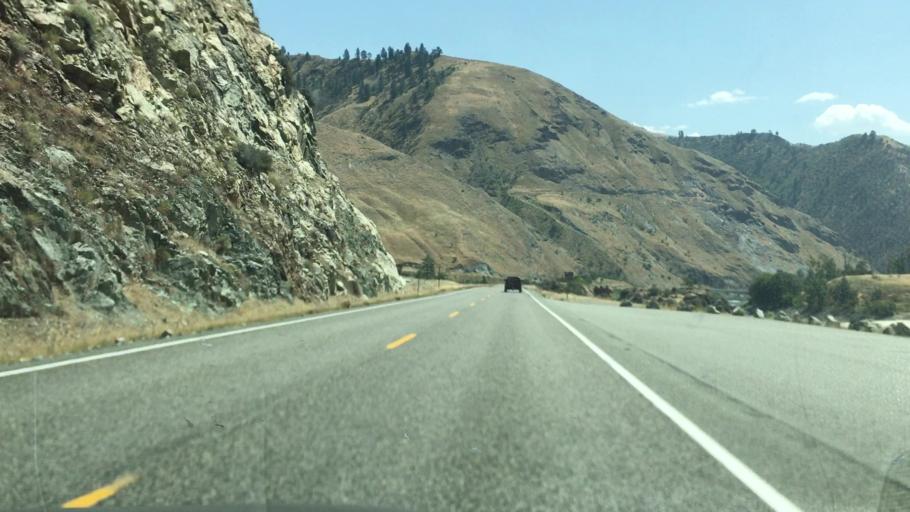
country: US
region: Idaho
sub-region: Idaho County
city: Grangeville
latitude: 45.6136
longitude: -116.2810
